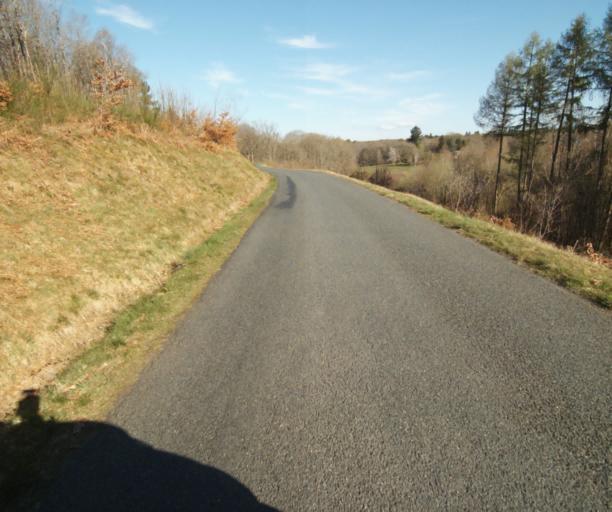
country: FR
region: Limousin
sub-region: Departement de la Correze
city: Correze
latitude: 45.2698
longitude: 1.8937
